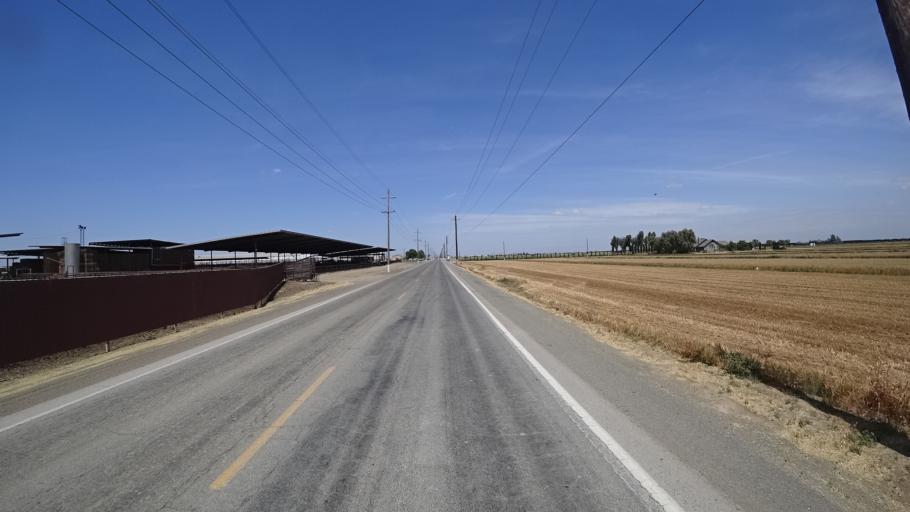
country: US
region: California
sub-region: Kings County
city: Home Garden
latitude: 36.2300
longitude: -119.6549
